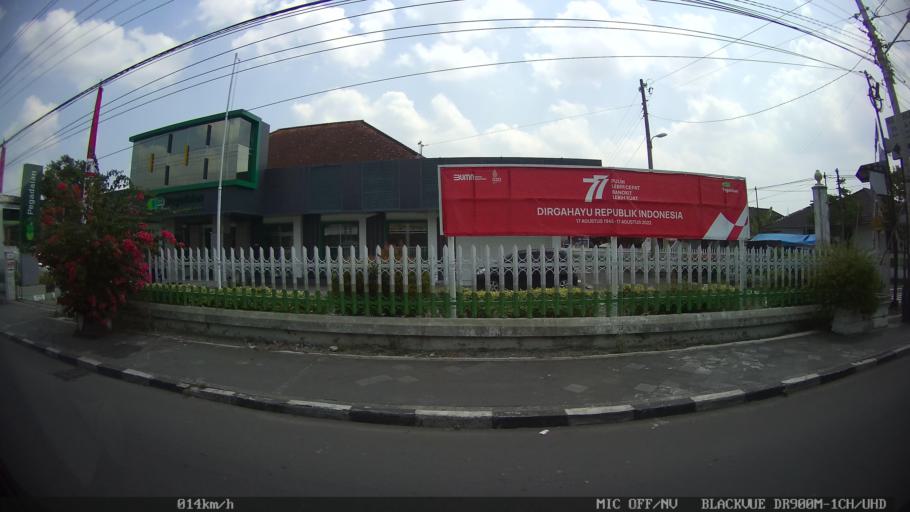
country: ID
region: Daerah Istimewa Yogyakarta
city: Yogyakarta
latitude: -7.8230
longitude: 110.4006
